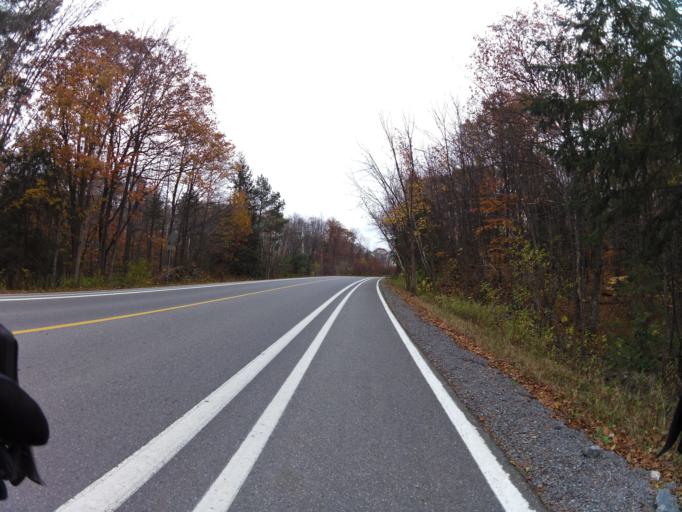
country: CA
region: Quebec
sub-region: Outaouais
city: Gatineau
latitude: 45.5091
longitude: -75.8212
